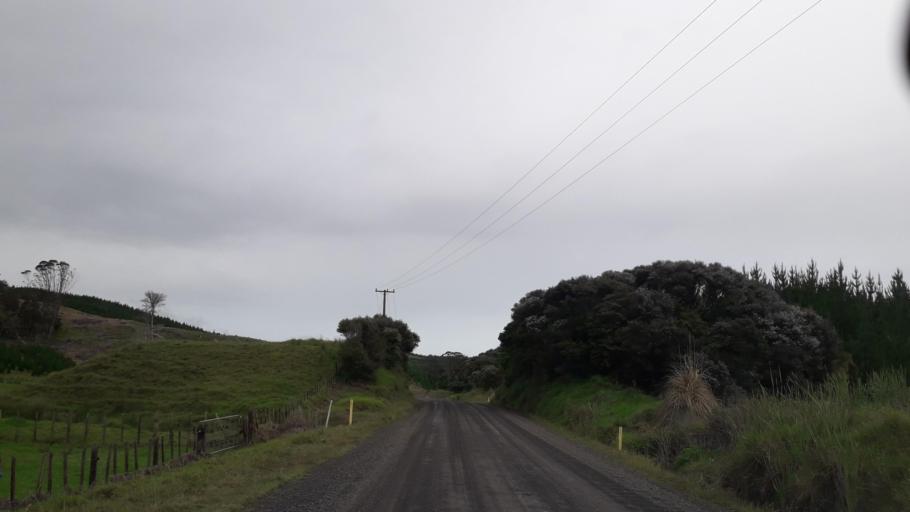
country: NZ
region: Northland
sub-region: Far North District
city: Ahipara
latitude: -35.4289
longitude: 173.3521
